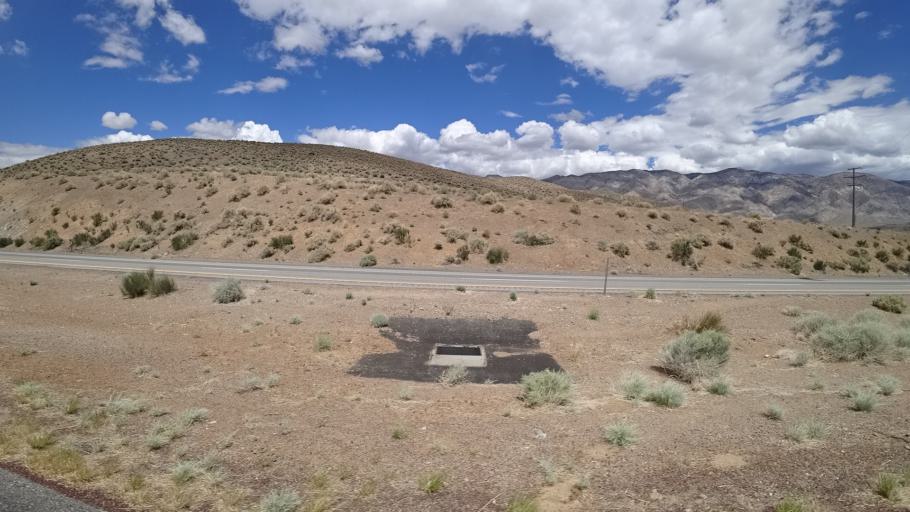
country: US
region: California
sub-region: Inyo County
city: Big Pine
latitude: 37.0582
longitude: -118.2371
